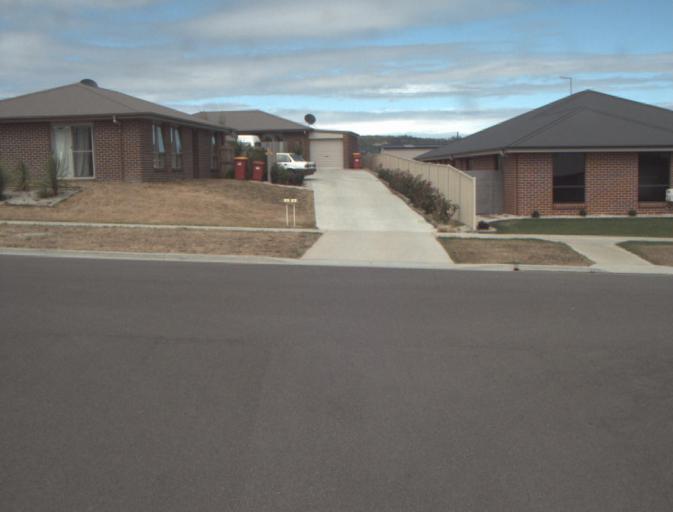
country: AU
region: Tasmania
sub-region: Launceston
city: Mayfield
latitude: -41.3886
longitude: 147.1128
